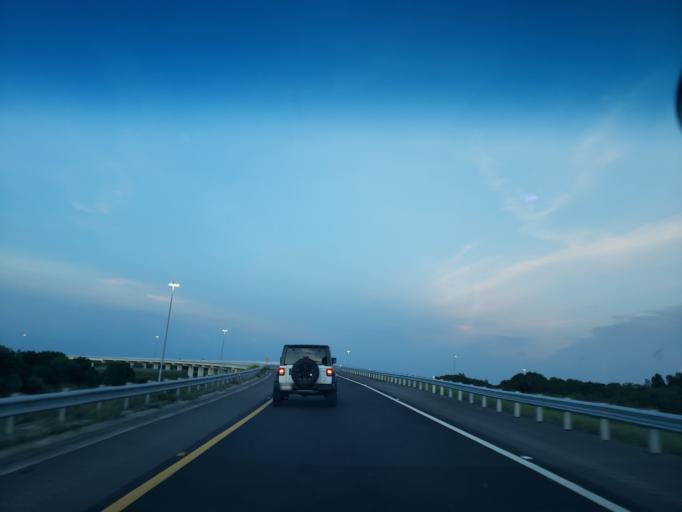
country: US
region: Florida
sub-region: Manatee County
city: Ellenton
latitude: 27.5848
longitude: -82.5204
